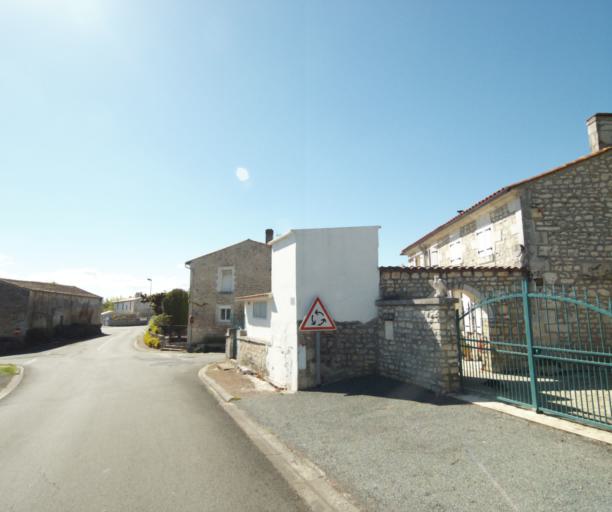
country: FR
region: Poitou-Charentes
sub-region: Departement de la Charente-Maritime
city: Bussac-sur-Charente
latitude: 45.8118
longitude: -0.6309
